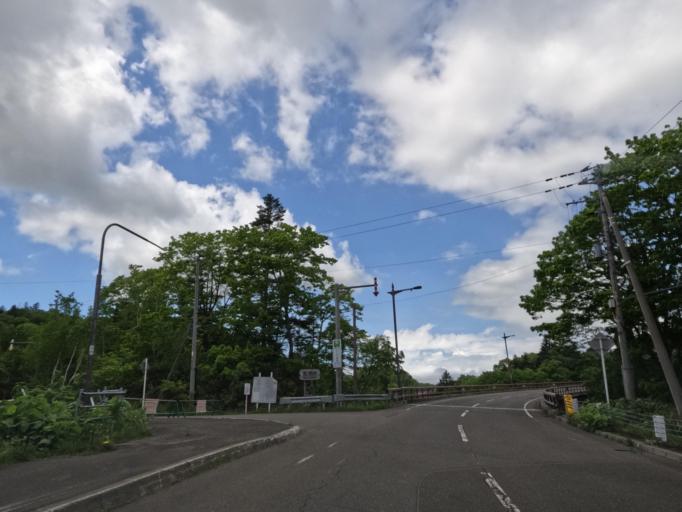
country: JP
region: Hokkaido
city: Tobetsu
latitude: 43.4740
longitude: 141.5945
